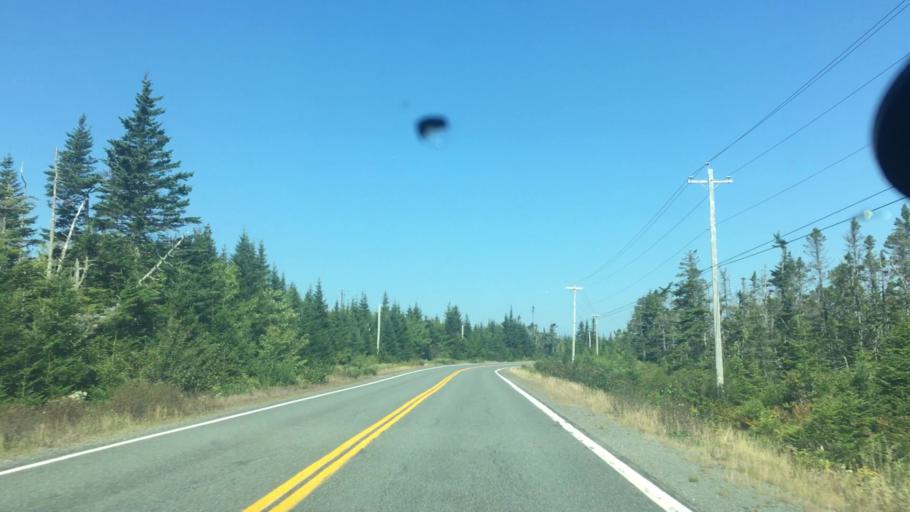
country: CA
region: Nova Scotia
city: Antigonish
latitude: 44.9854
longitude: -62.0967
